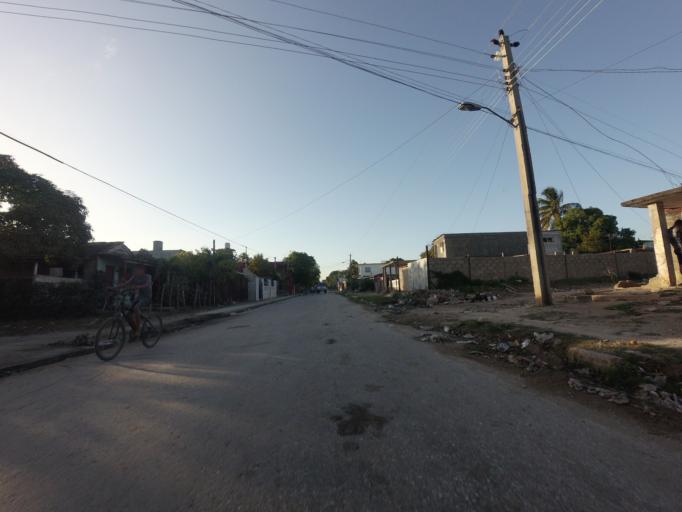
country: CU
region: Ciego de Avila
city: Ciego de Avila
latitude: 21.8306
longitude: -78.7547
